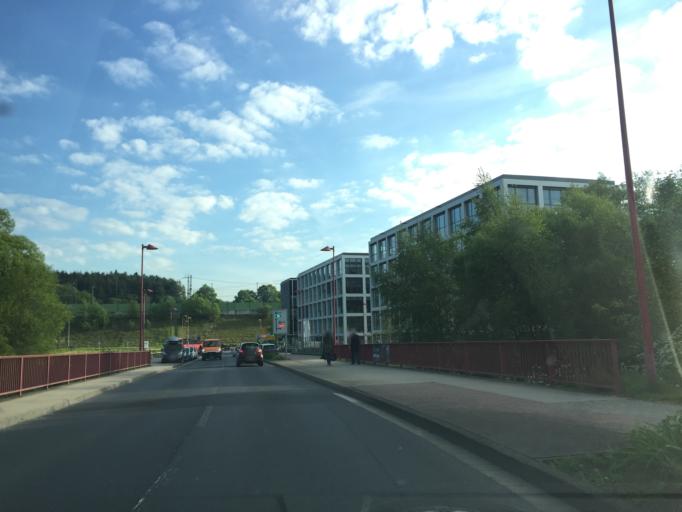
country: DE
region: Rheinland-Pfalz
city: Montabaur
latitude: 50.4428
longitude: 7.8213
